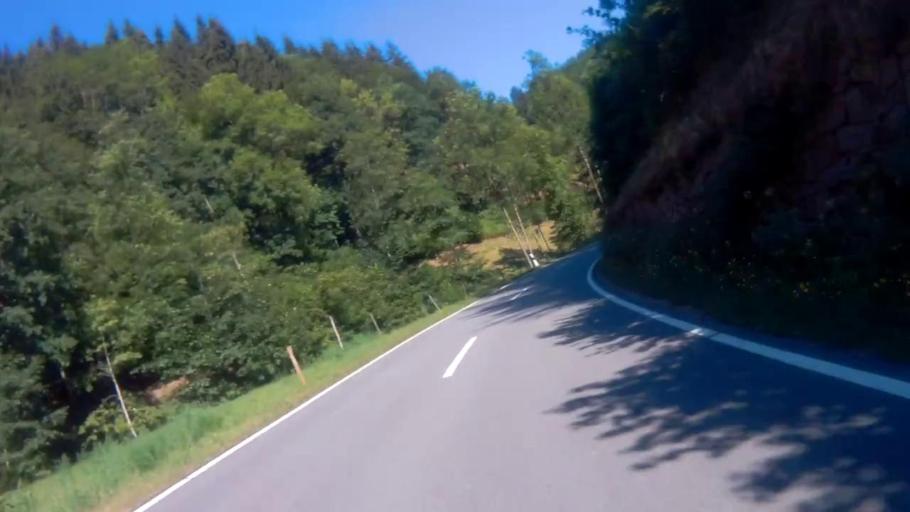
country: DE
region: Baden-Wuerttemberg
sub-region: Freiburg Region
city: Zell im Wiesental
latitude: 47.7340
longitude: 7.7698
